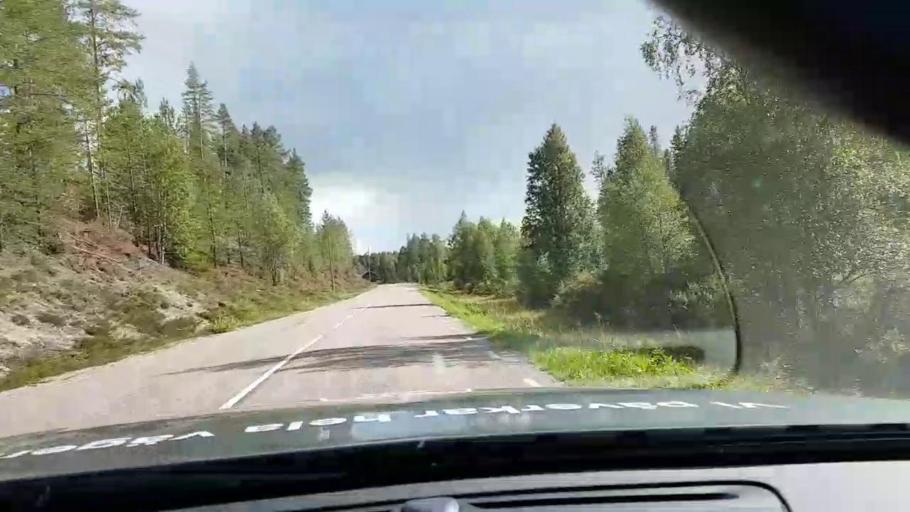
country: SE
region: Vaesterbotten
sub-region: Asele Kommun
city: Asele
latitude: 63.8657
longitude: 17.3649
